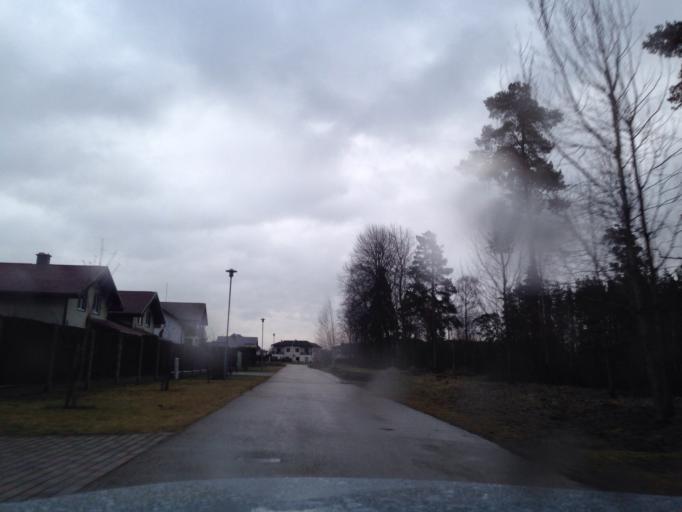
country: LV
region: Marupe
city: Marupe
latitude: 56.8881
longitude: 24.0319
